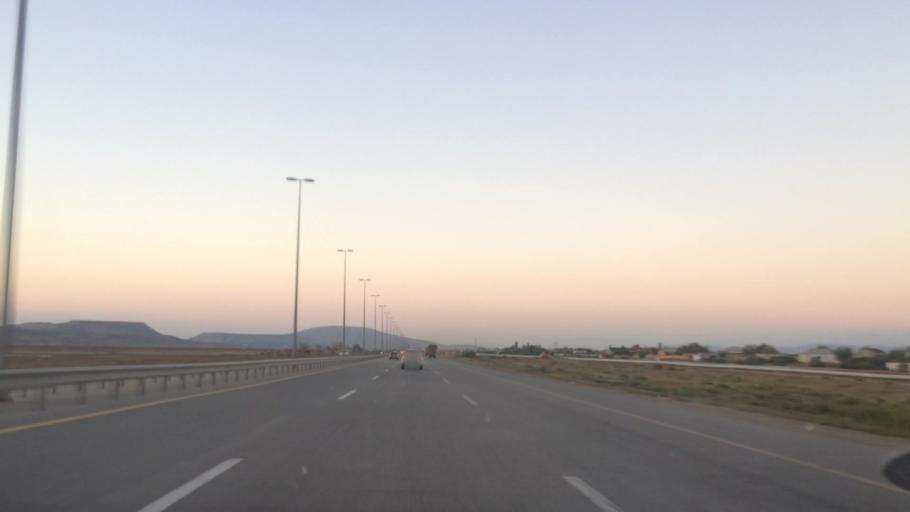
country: AZ
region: Baki
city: Qobustan
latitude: 40.0131
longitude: 49.4268
